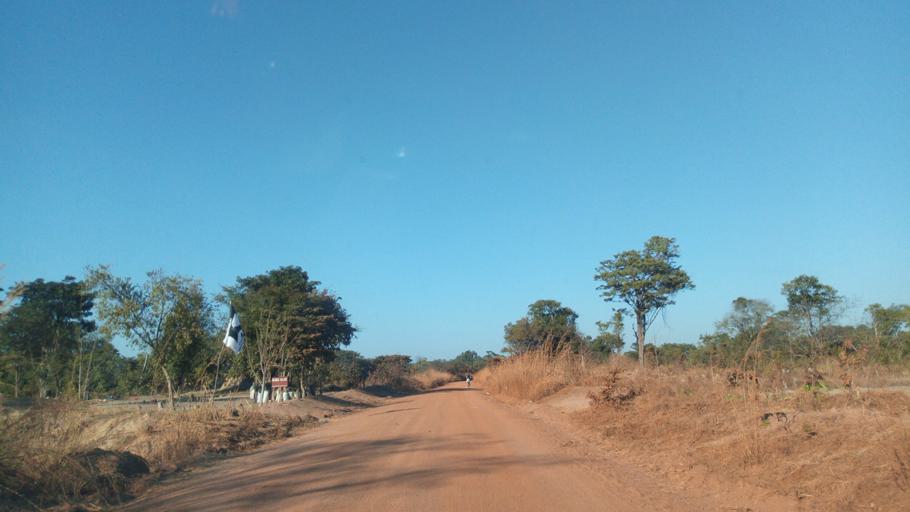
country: ZM
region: Luapula
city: Mwense
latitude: -10.4944
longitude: 28.4850
